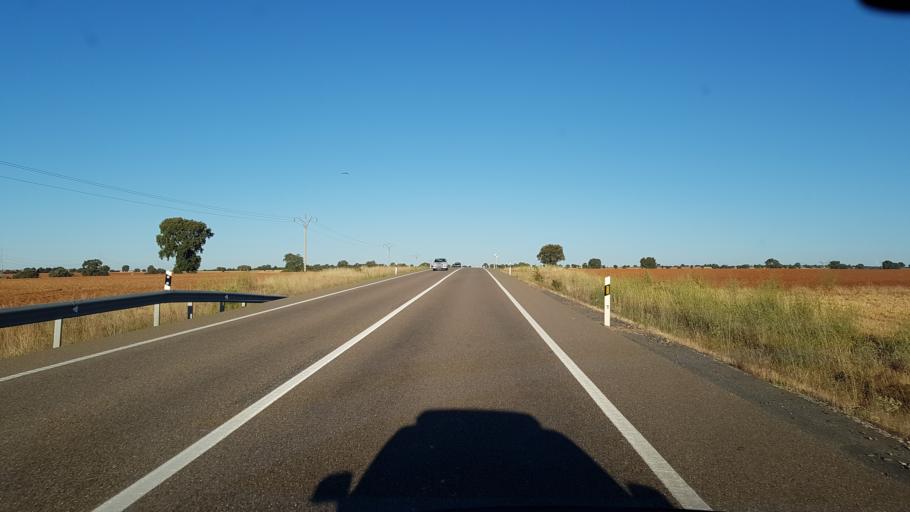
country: ES
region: Castille and Leon
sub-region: Provincia de Zamora
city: Palacios del Pan
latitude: 41.5461
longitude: -5.8923
